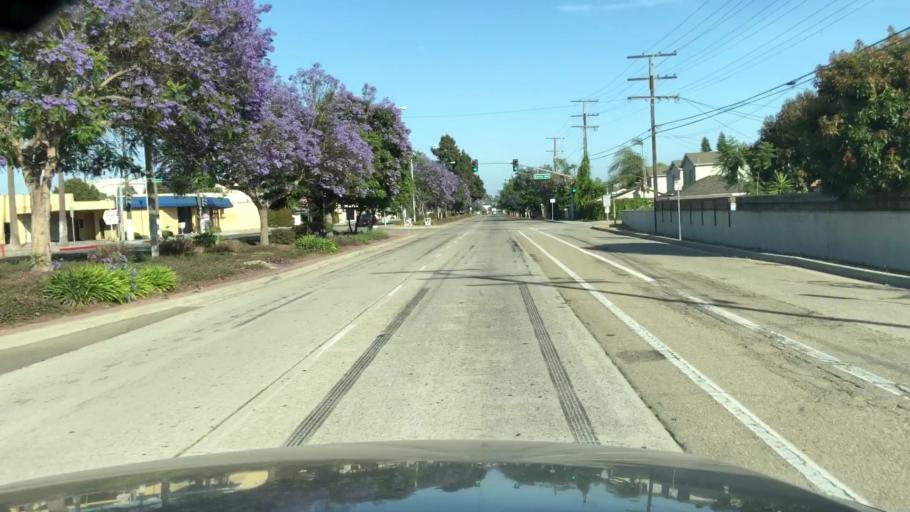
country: US
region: California
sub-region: Ventura County
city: Ventura
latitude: 34.2696
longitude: -119.2543
